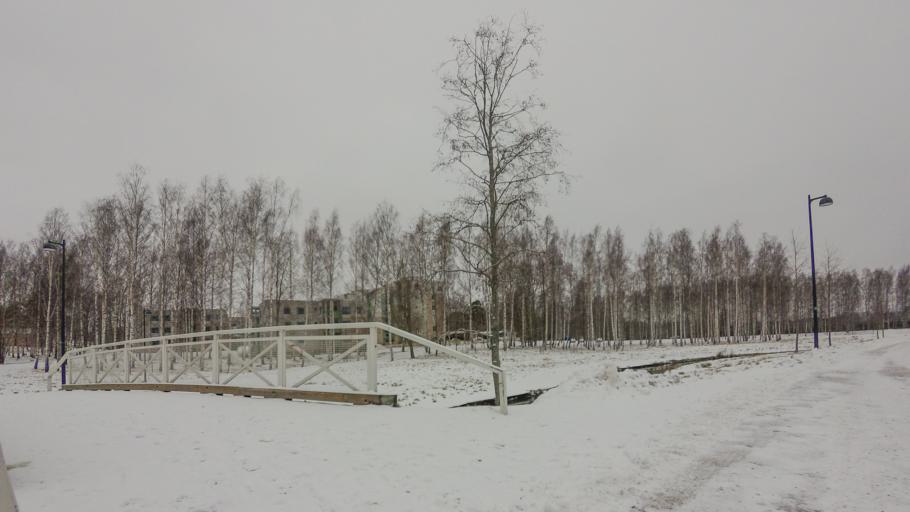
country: FI
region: Uusimaa
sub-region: Helsinki
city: Vantaa
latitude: 60.2005
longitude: 25.0695
